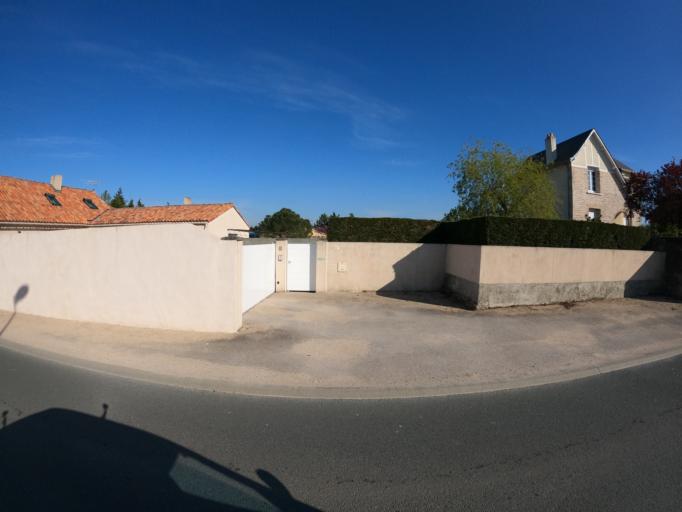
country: FR
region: Pays de la Loire
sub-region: Departement de la Vendee
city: Beaurepaire
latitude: 46.9087
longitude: -1.1312
